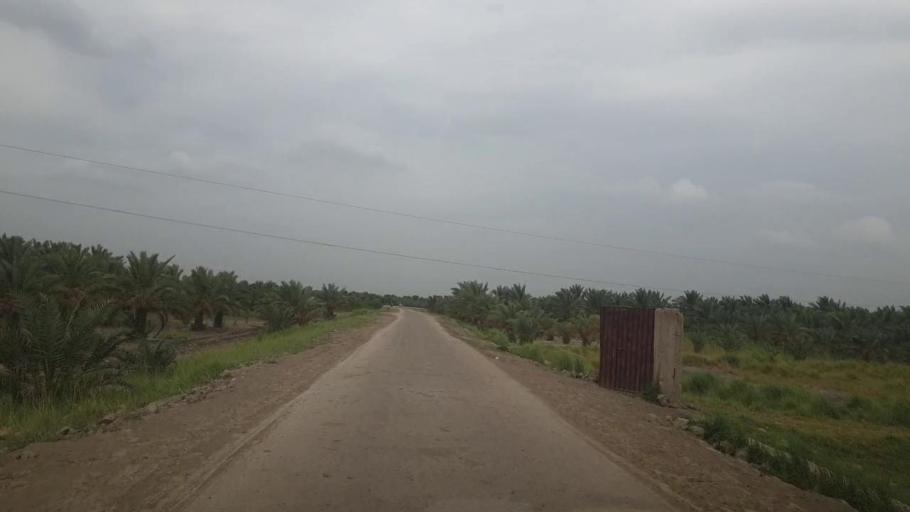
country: PK
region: Sindh
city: Khairpur
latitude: 27.5733
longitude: 68.7340
